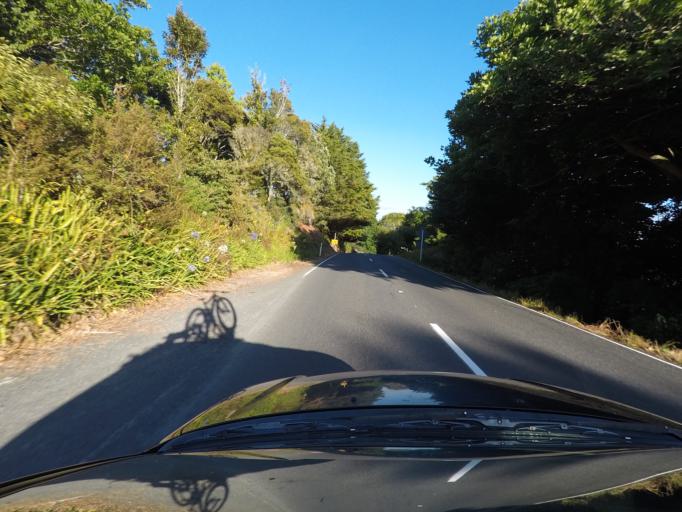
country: NZ
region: Northland
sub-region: Whangarei
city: Whangarei
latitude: -35.6552
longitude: 174.3097
